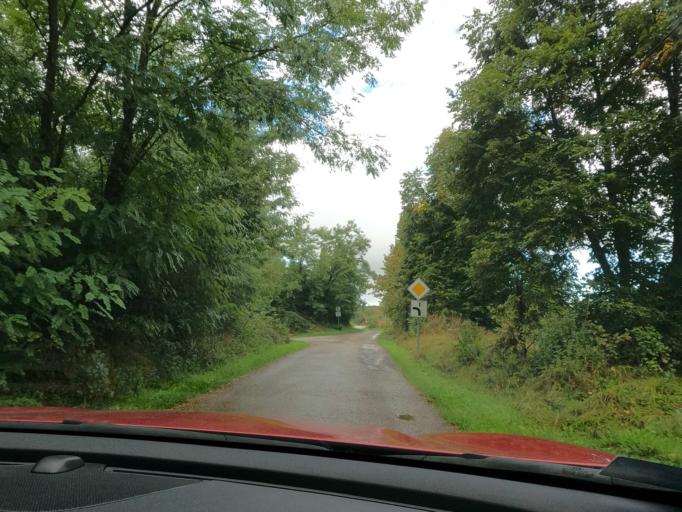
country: HR
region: Sisacko-Moslavacka
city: Petrinja
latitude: 45.3276
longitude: 16.2252
